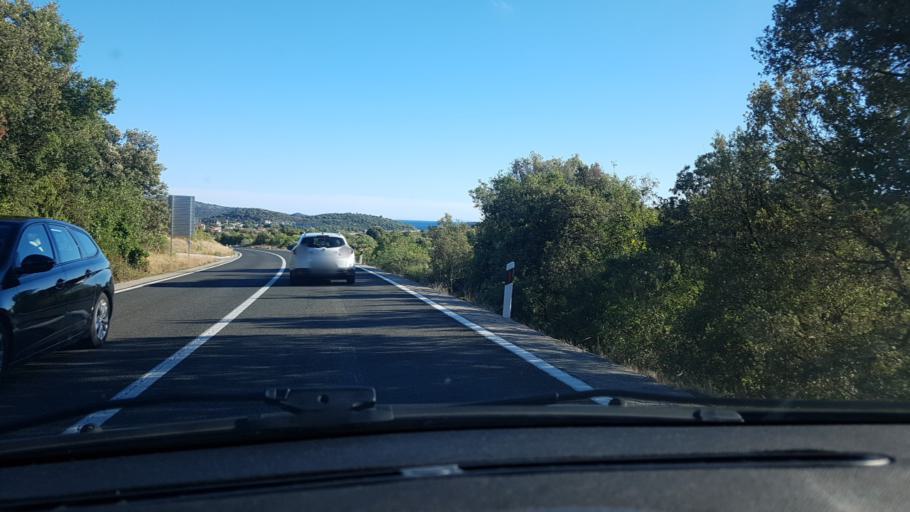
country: HR
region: Sibensko-Kniniska
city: Rogoznica
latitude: 43.5501
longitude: 15.9606
